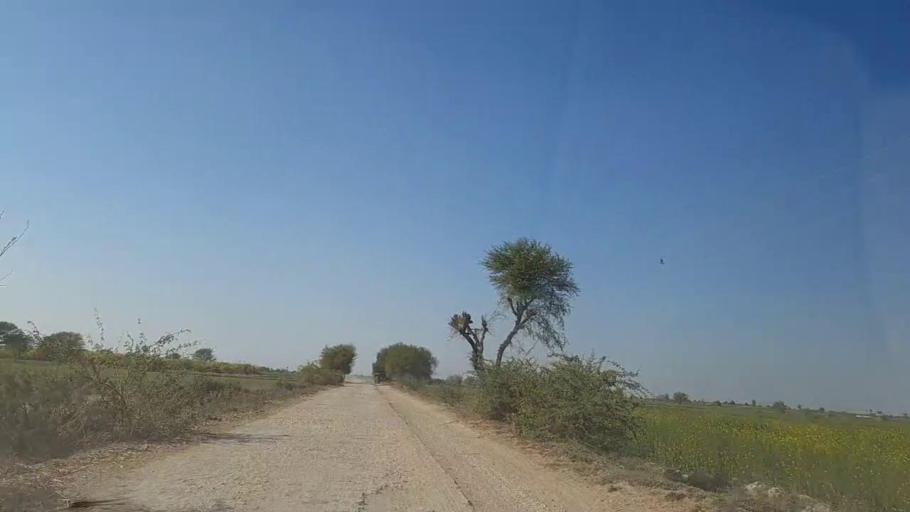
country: PK
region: Sindh
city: Digri
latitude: 25.1640
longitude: 69.0267
